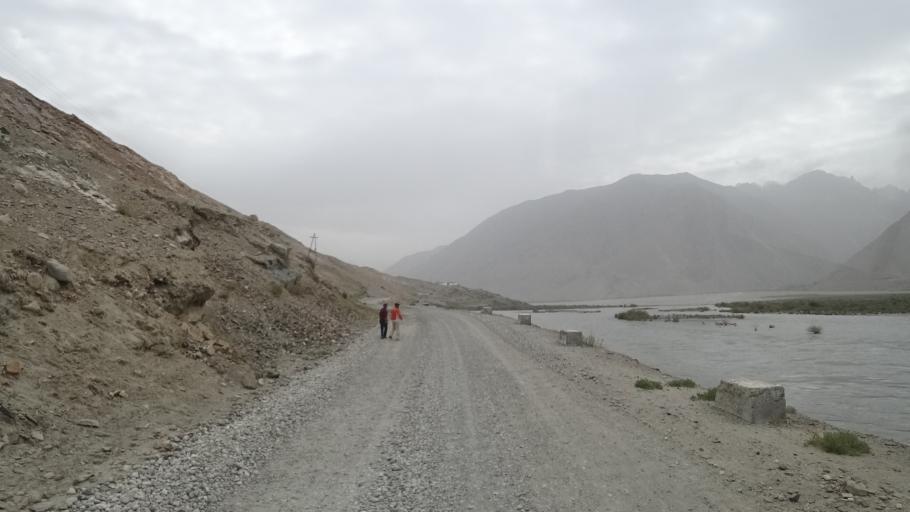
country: AF
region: Badakhshan
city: Khandud
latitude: 37.0051
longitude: 72.5354
